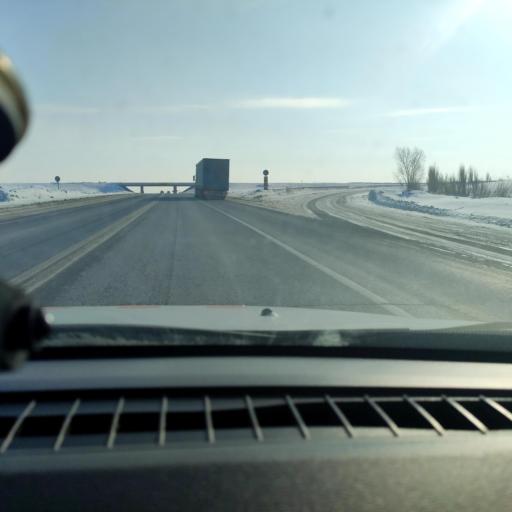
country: RU
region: Samara
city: Petra-Dubrava
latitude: 53.3431
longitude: 50.4512
